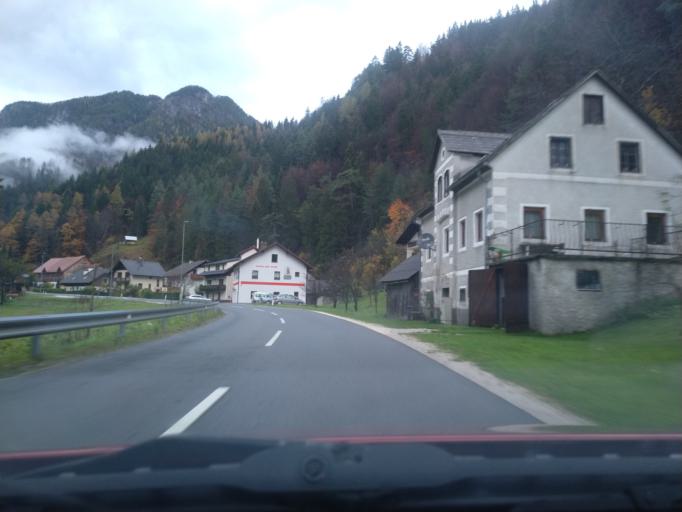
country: SI
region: Solcava
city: Solcava
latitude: 46.4184
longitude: 14.6973
